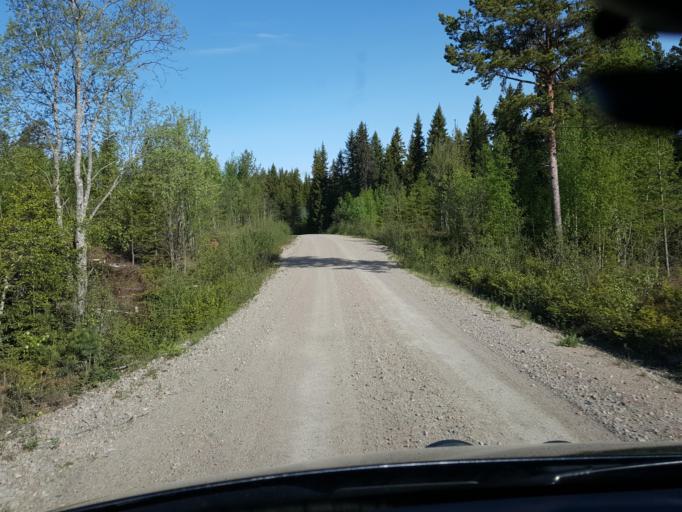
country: SE
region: Vaesternorrland
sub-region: Ange Kommun
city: Ange
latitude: 62.1834
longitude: 15.6158
